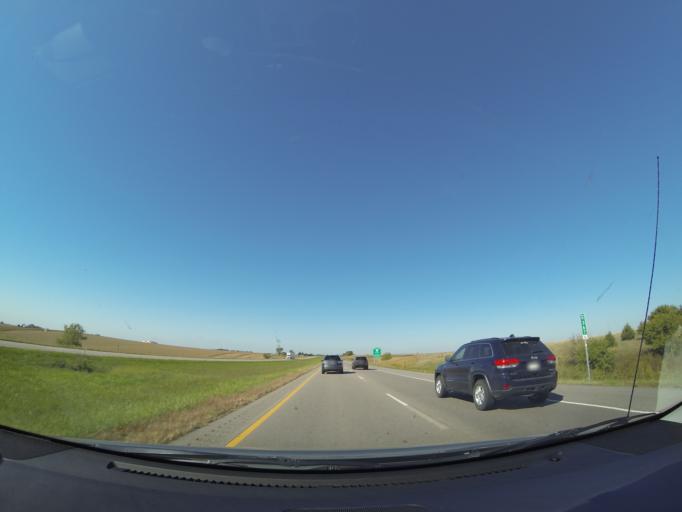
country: US
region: Nebraska
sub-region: Saline County
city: Friend
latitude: 40.8218
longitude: -97.3210
